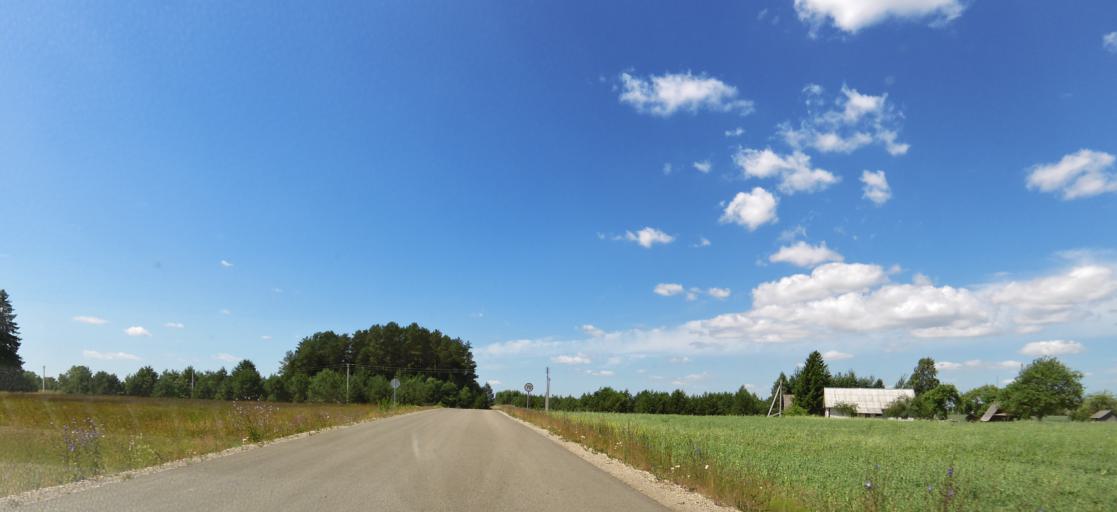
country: LT
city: Kupiskis
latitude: 55.9340
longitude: 24.9035
